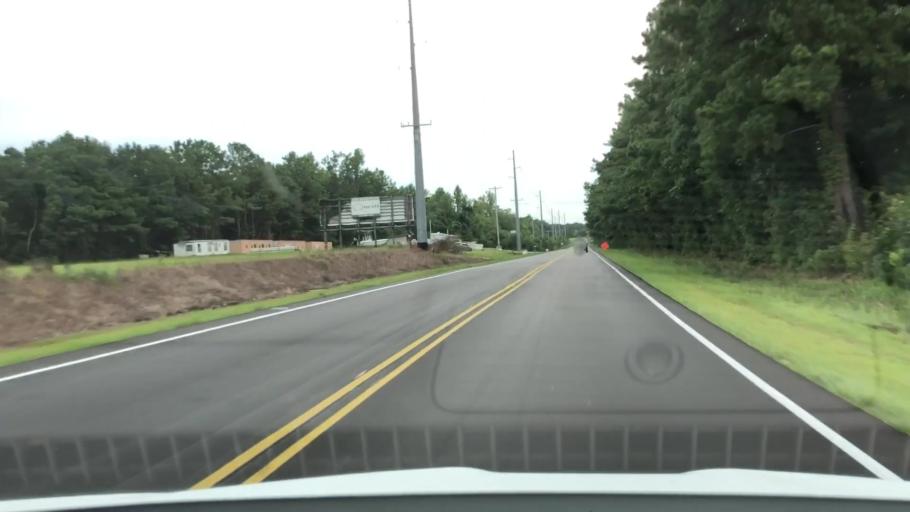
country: US
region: North Carolina
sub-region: Onslow County
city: Swansboro
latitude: 34.7936
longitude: -77.1315
